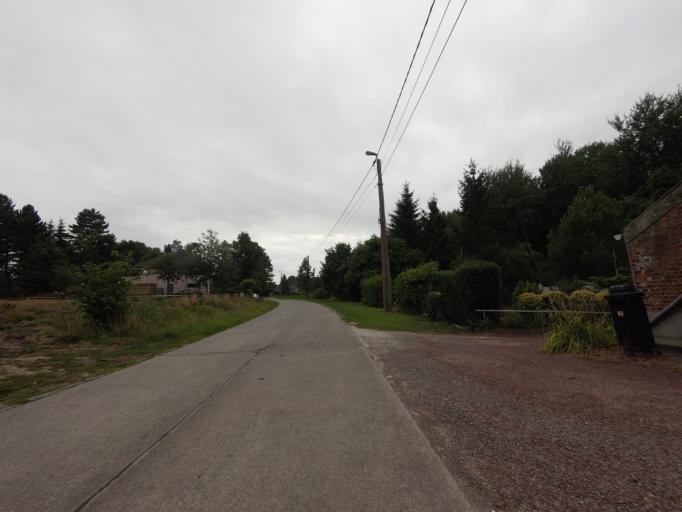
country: BE
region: Flanders
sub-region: Provincie Antwerpen
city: Duffel
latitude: 51.1019
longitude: 4.5241
